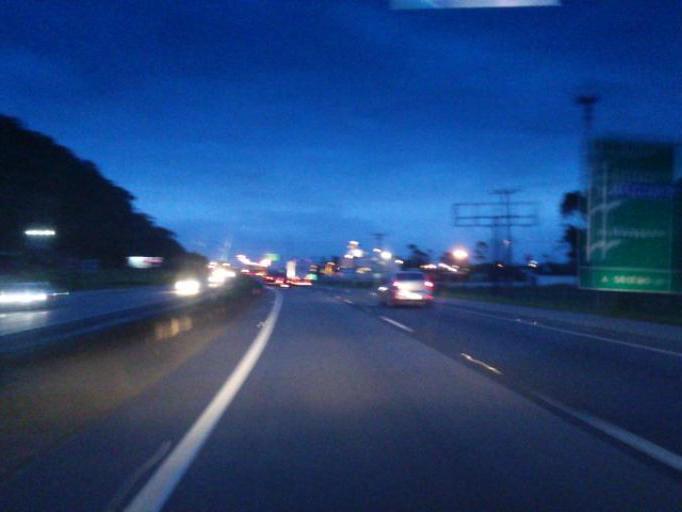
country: BR
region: Santa Catarina
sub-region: Navegantes
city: Navegantes
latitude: -26.8368
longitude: -48.7116
